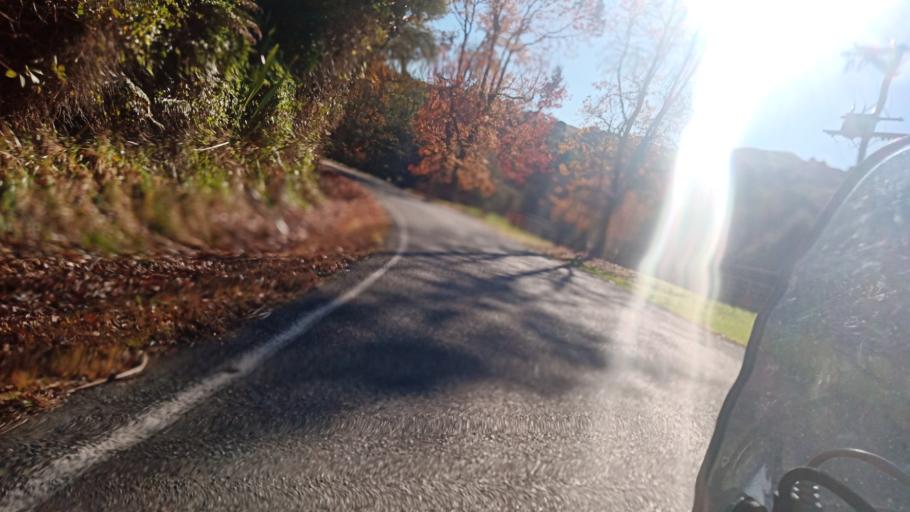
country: NZ
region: Hawke's Bay
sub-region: Wairoa District
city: Wairoa
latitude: -38.8192
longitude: 177.2955
